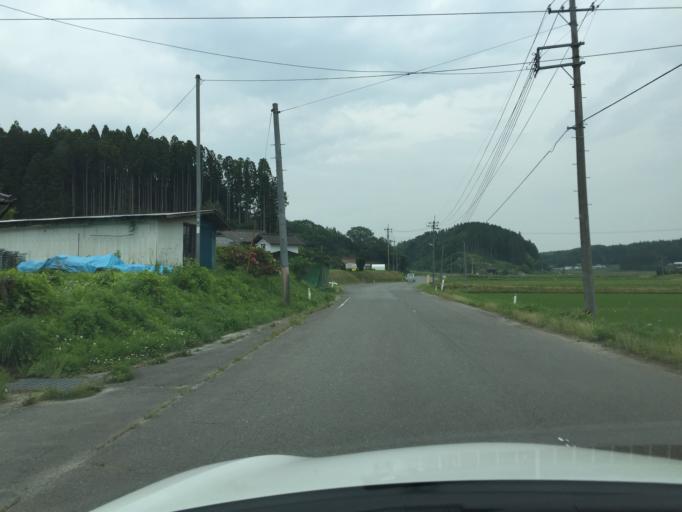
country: JP
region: Fukushima
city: Iwaki
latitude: 37.1873
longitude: 140.7182
